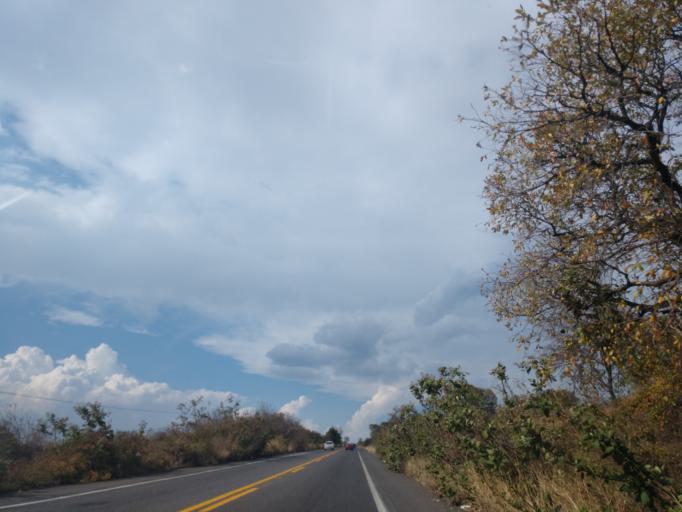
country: MX
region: Jalisco
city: La Manzanilla de la Paz
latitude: 20.0640
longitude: -103.1715
